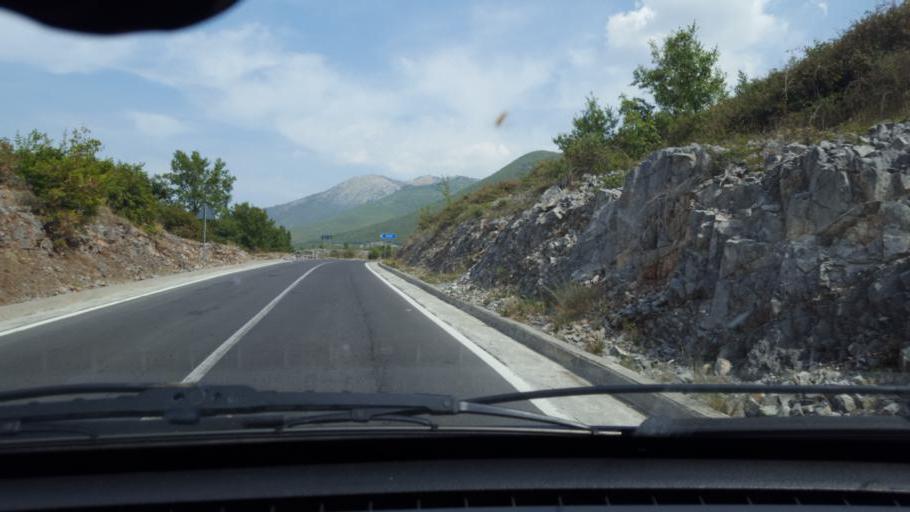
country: AL
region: Shkoder
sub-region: Rrethi i Malesia e Madhe
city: Hot
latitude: 42.3693
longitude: 19.4686
